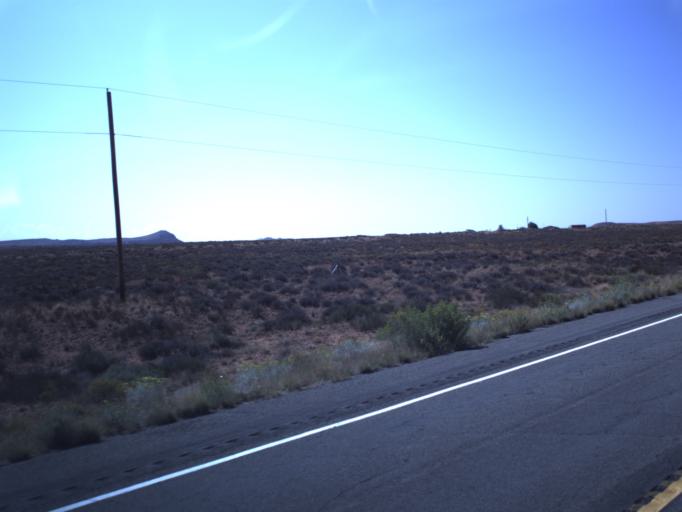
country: US
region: Utah
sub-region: San Juan County
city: Blanding
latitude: 37.0204
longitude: -109.6067
